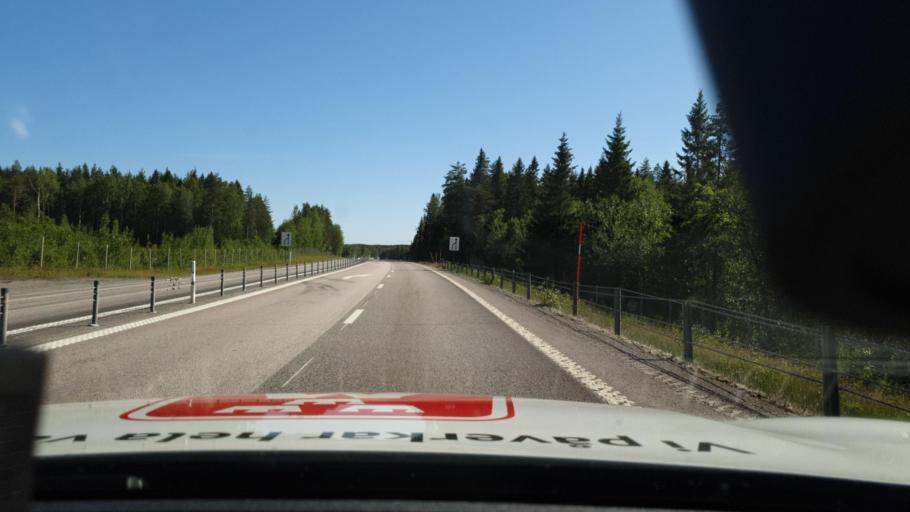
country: SE
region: Norrbotten
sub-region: Lulea Kommun
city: Ranea
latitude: 65.7617
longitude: 22.1674
